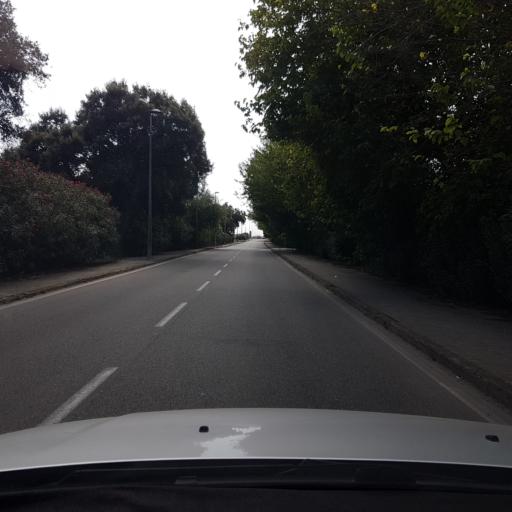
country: IT
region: Sardinia
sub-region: Provincia di Oristano
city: Donigala Fenugheddu
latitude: 39.9239
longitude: 8.5803
